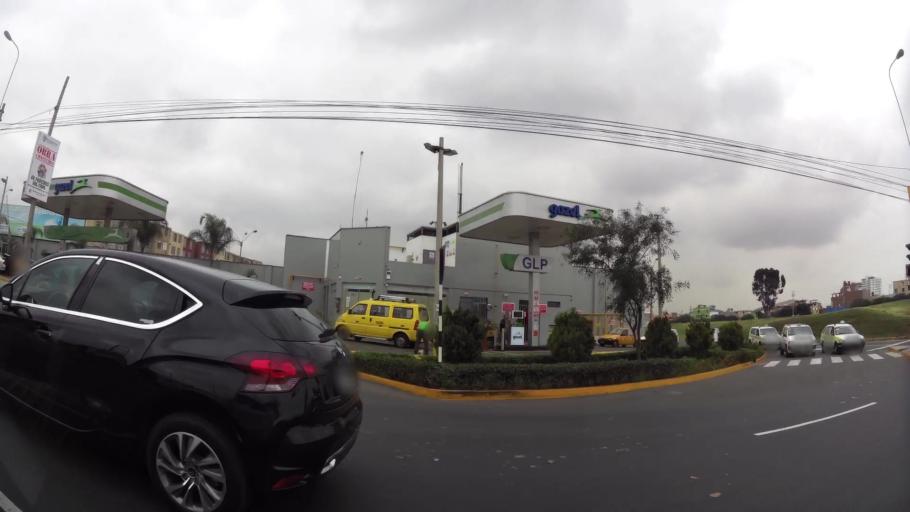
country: PE
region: Lima
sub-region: Lima
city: Surco
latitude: -12.1527
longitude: -76.9896
